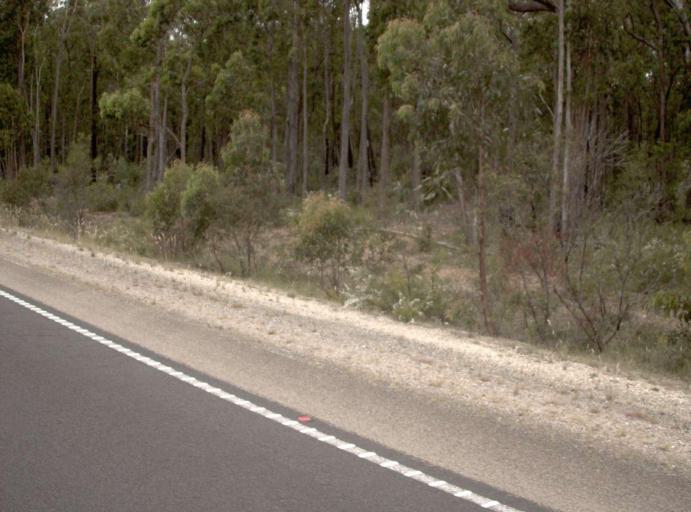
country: AU
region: Victoria
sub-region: East Gippsland
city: Lakes Entrance
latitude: -37.7025
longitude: 147.9931
